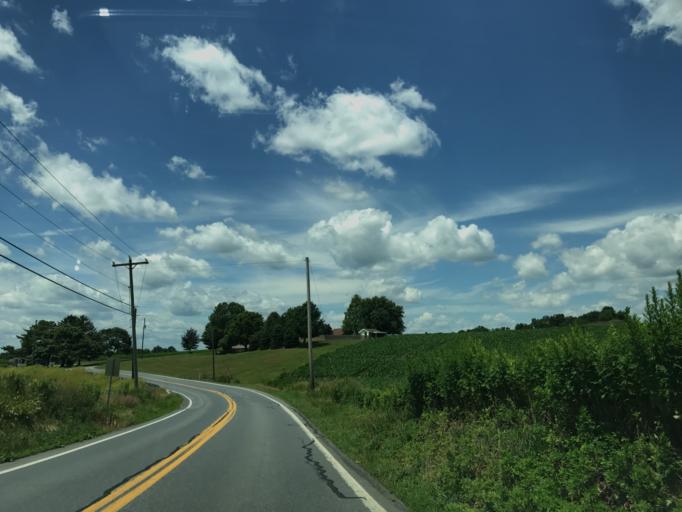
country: US
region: Pennsylvania
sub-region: Lancaster County
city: Mountville
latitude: 39.9619
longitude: -76.4398
